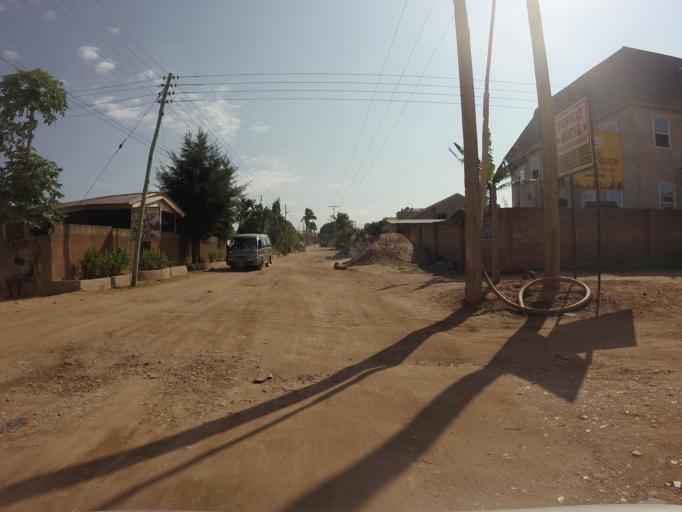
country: GH
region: Greater Accra
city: Dome
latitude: 5.6395
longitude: -0.2353
